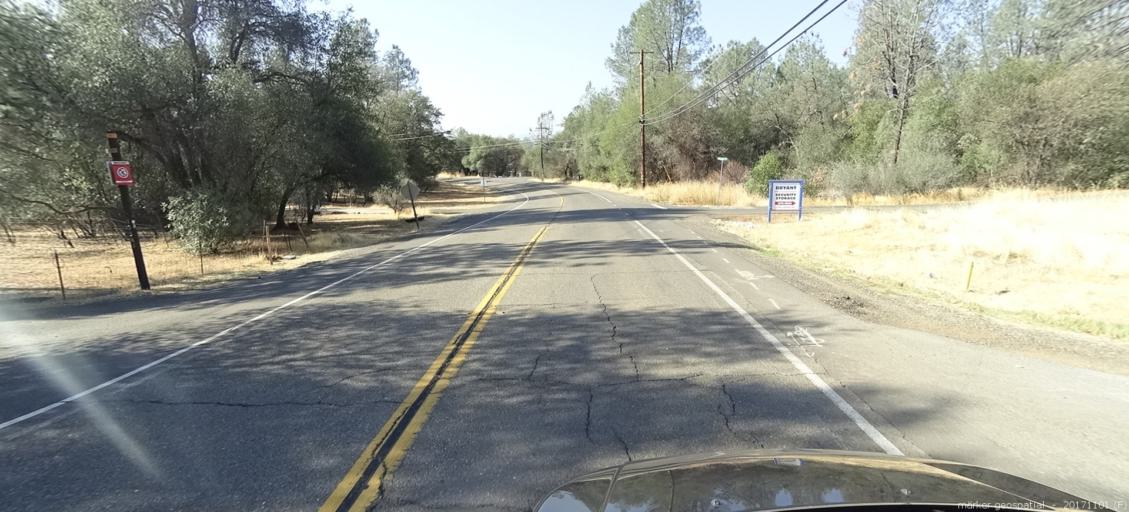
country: US
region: California
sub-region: Shasta County
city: Shasta Lake
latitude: 40.6856
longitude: -122.3429
